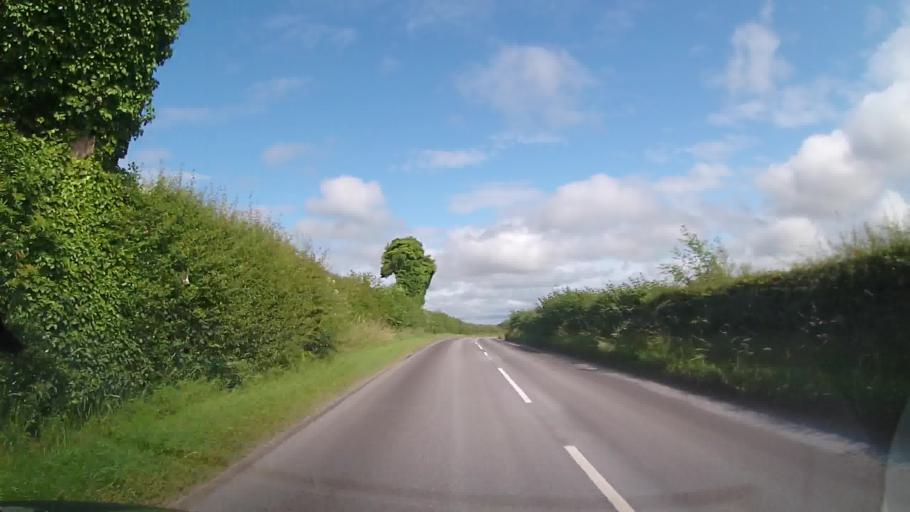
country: GB
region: England
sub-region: Shropshire
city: Pant
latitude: 52.8101
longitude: -3.0367
